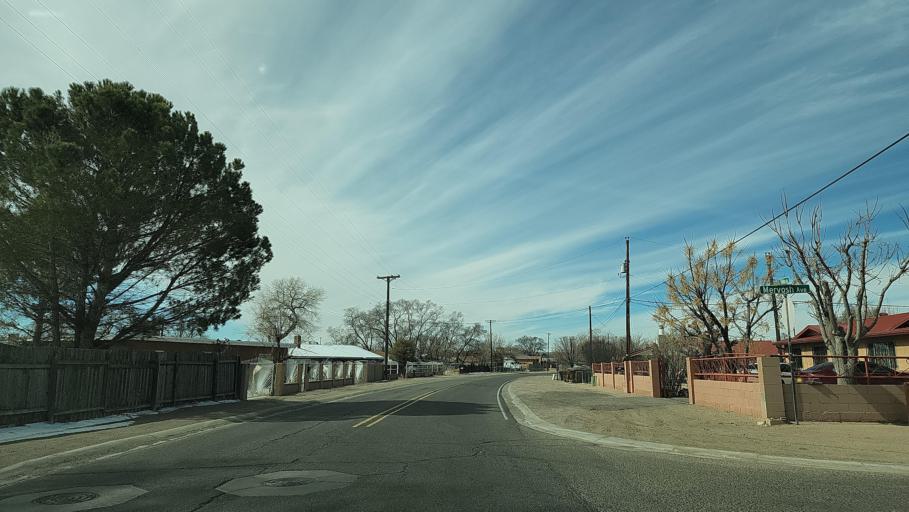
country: US
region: New Mexico
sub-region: Bernalillo County
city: South Valley
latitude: 35.0368
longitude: -106.6836
